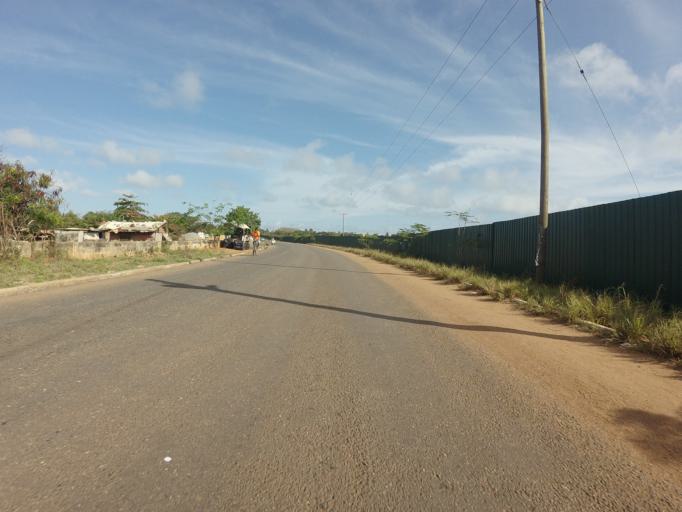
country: GH
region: Greater Accra
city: Teshi Old Town
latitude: 5.5681
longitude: -0.1411
